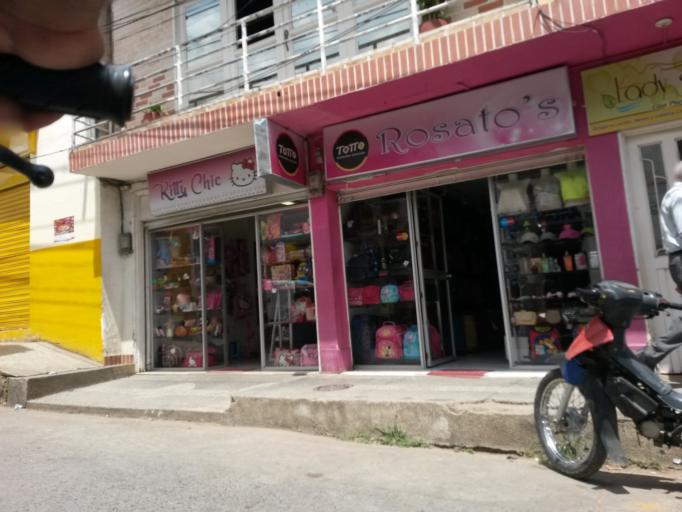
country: CO
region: Cauca
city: Santander de Quilichao
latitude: 3.0075
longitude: -76.4840
